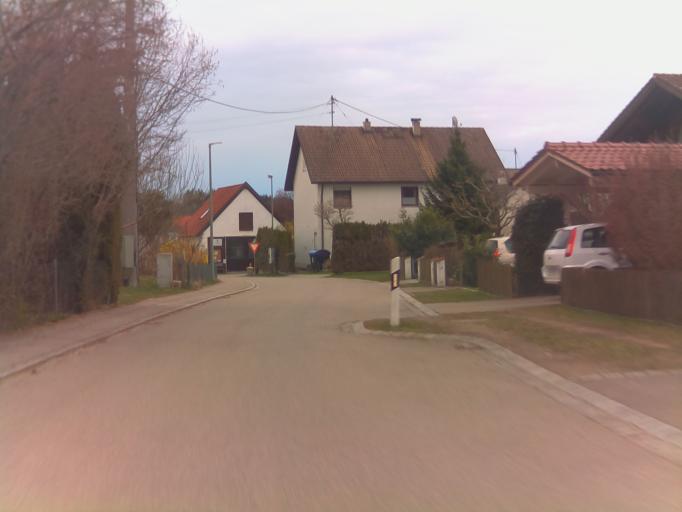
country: DE
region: Bavaria
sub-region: Upper Bavaria
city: Penzing
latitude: 48.0818
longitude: 10.9671
